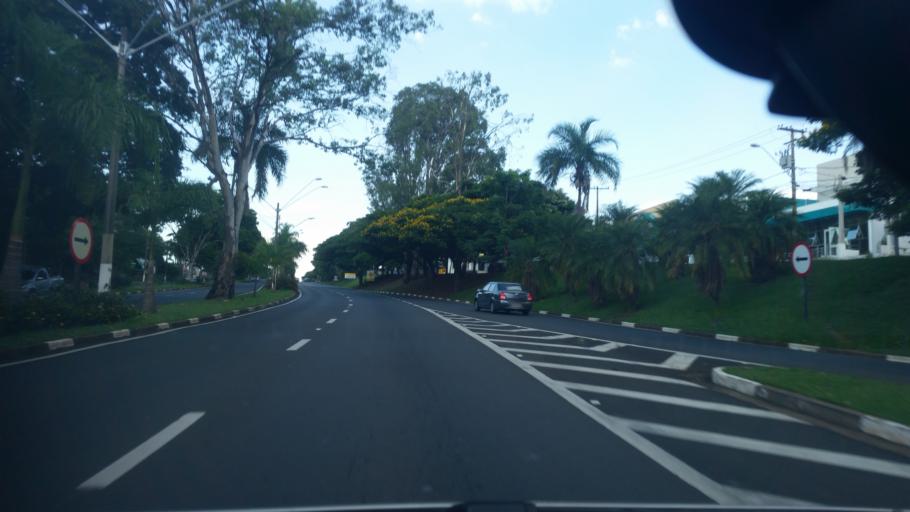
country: BR
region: Sao Paulo
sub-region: Campinas
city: Campinas
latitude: -22.8717
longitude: -47.0450
